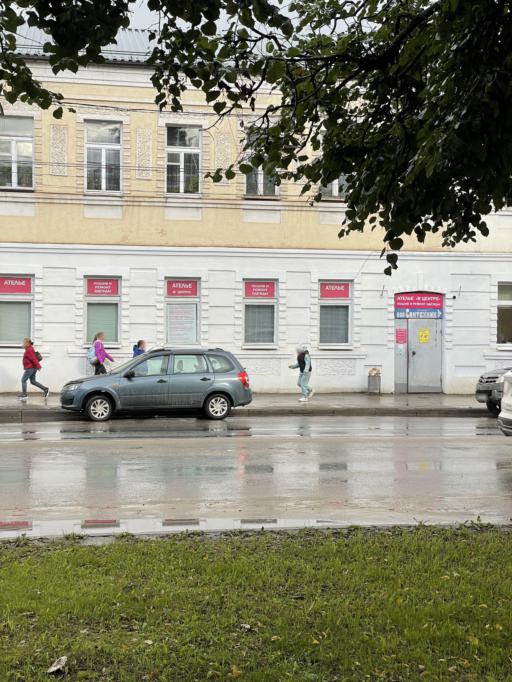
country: RU
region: Tverskaya
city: Vyshniy Volochek
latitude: 57.5831
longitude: 34.5596
